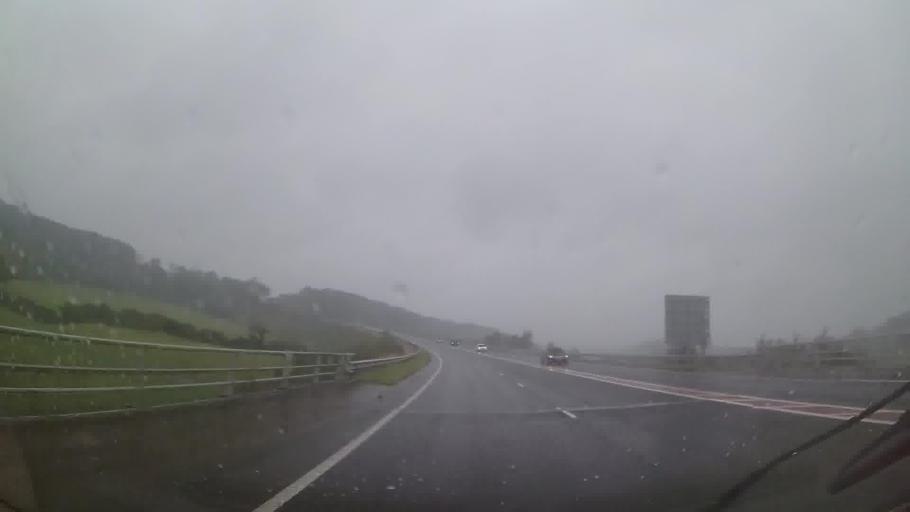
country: GB
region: Wales
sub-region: Carmarthenshire
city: Llanddowror
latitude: 51.8043
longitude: -4.5333
